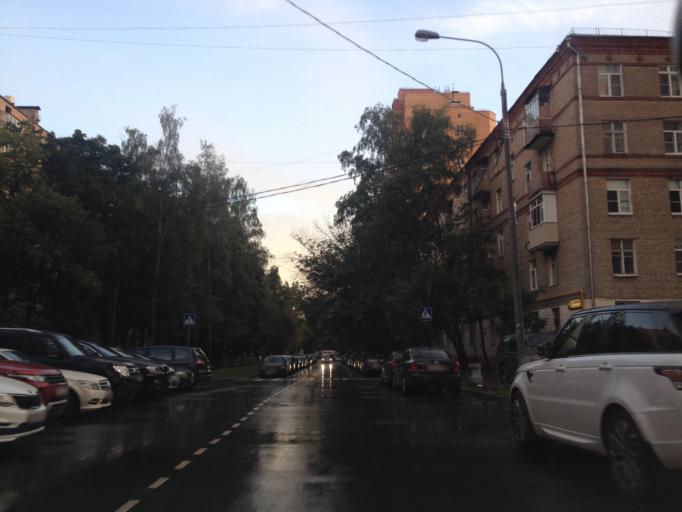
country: RU
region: Moskovskaya
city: Izmaylovo
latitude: 55.7915
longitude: 37.7883
